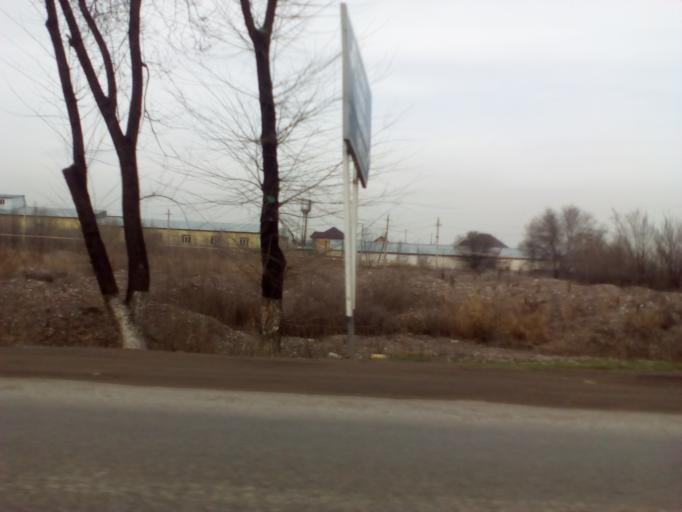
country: KZ
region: Almaty Oblysy
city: Burunday
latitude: 43.2272
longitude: 76.7458
